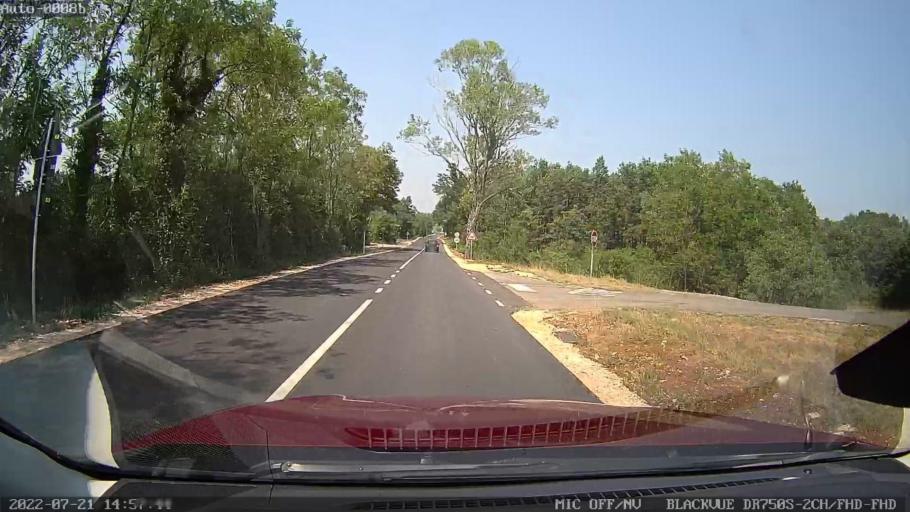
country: HR
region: Istarska
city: Pazin
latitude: 45.2109
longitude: 13.9544
